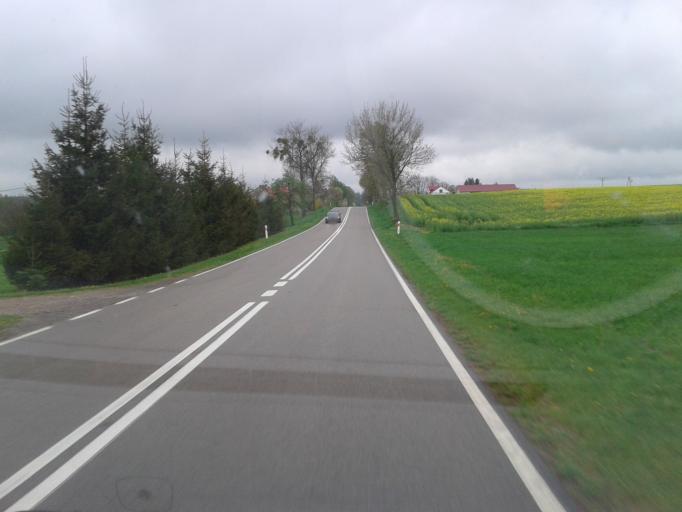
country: PL
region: Lublin Voivodeship
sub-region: Powiat tomaszowski
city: Telatyn
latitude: 50.5351
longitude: 23.9201
